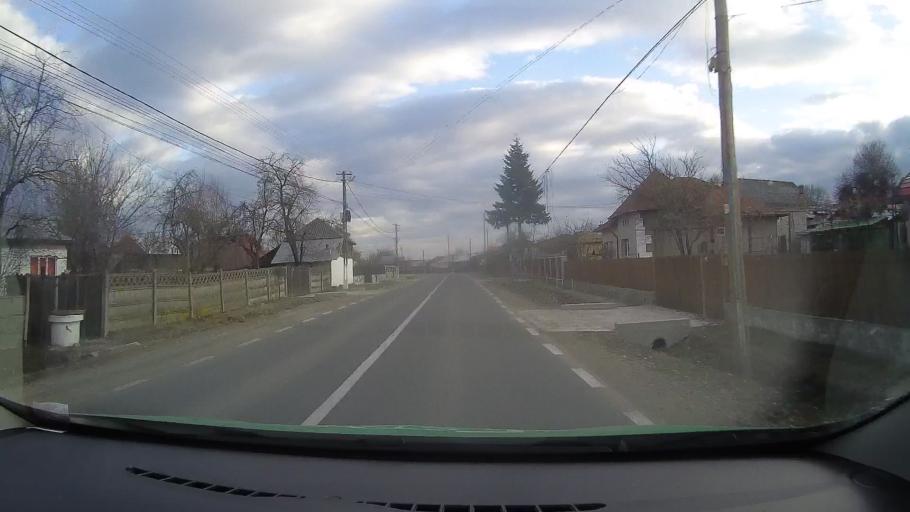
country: RO
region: Dambovita
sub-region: Comuna I. L. Caragiale
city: Ghirdoveni
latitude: 44.9331
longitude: 25.6854
